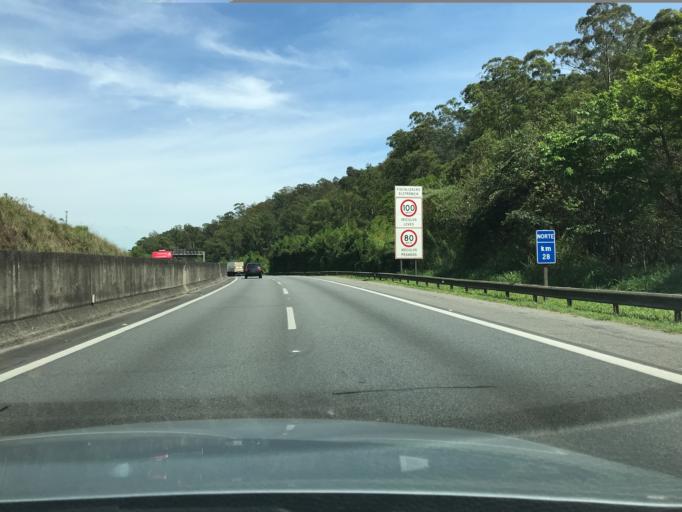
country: BR
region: Sao Paulo
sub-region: Caieiras
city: Caieiras
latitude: -23.4112
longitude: -46.8108
